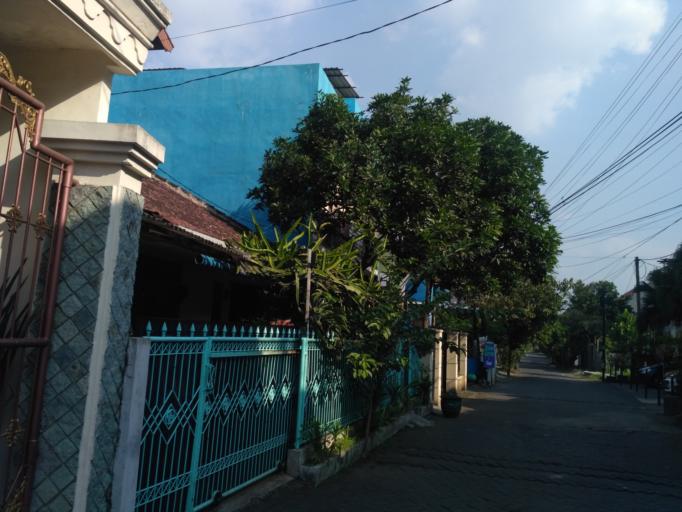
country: ID
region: East Java
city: Malang
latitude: -7.9550
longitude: 112.6086
